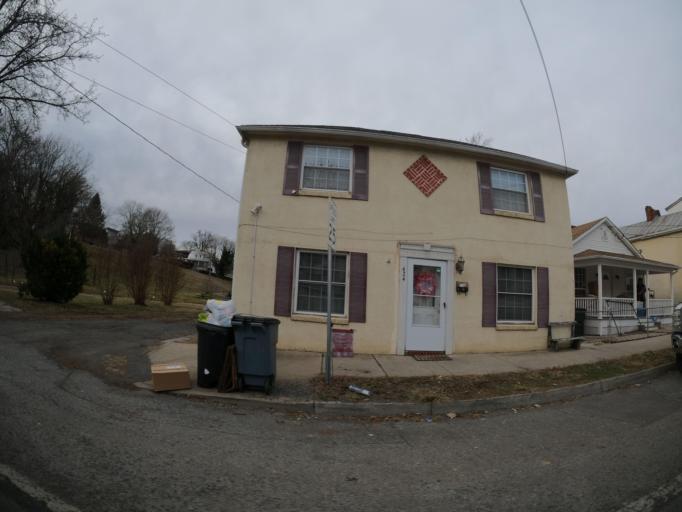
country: US
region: West Virginia
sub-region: Jefferson County
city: Charles Town
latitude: 39.2863
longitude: -77.8628
